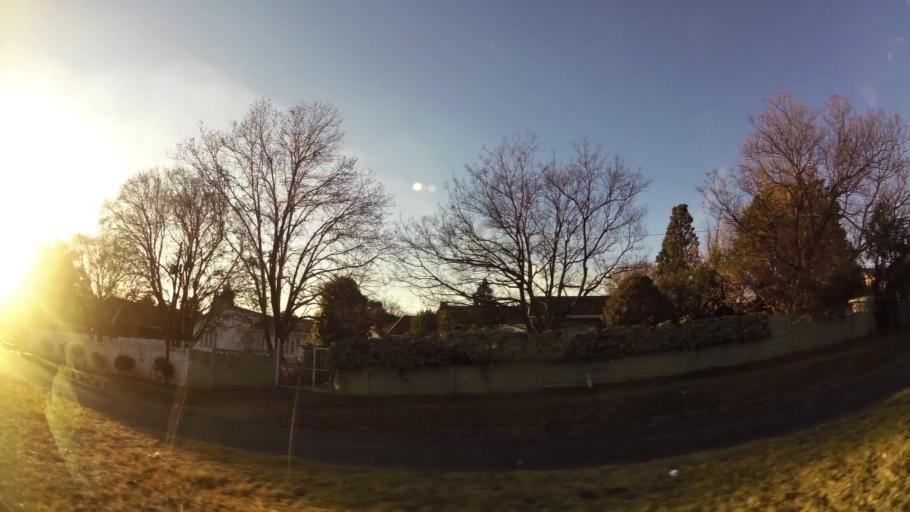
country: ZA
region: Gauteng
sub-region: City of Johannesburg Metropolitan Municipality
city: Roodepoort
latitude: -26.1580
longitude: 27.8877
